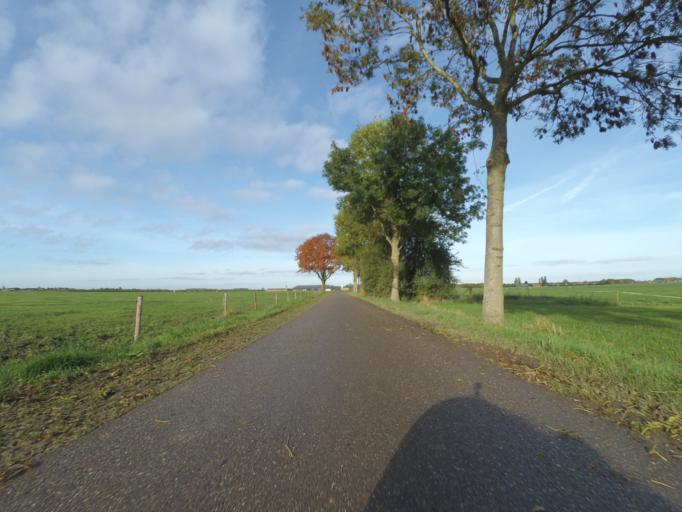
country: NL
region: Utrecht
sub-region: Gemeente Utrechtse Heuvelrug
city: Driebergen-Rijsenburg
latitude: 52.0060
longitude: 5.2535
